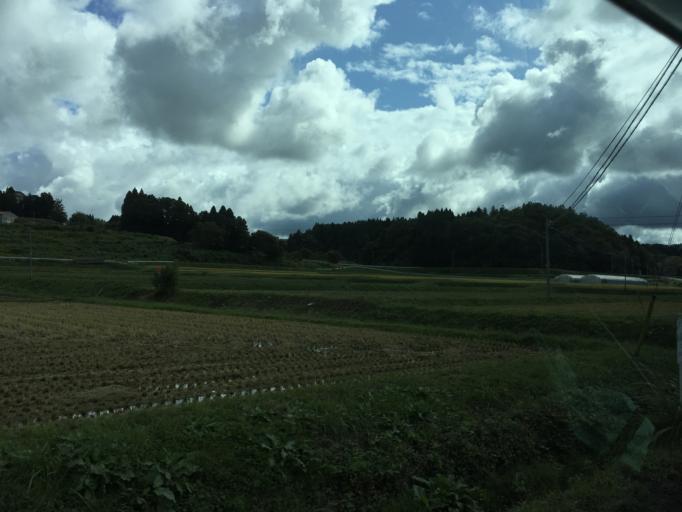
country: JP
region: Iwate
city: Ichinoseki
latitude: 38.8475
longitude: 141.3398
